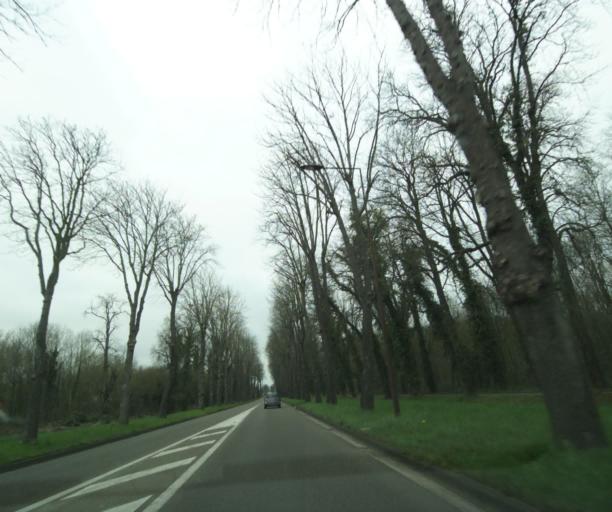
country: FR
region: Ile-de-France
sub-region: Departement des Yvelines
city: Saint-Germain-en-Laye
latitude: 48.9069
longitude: 2.0794
